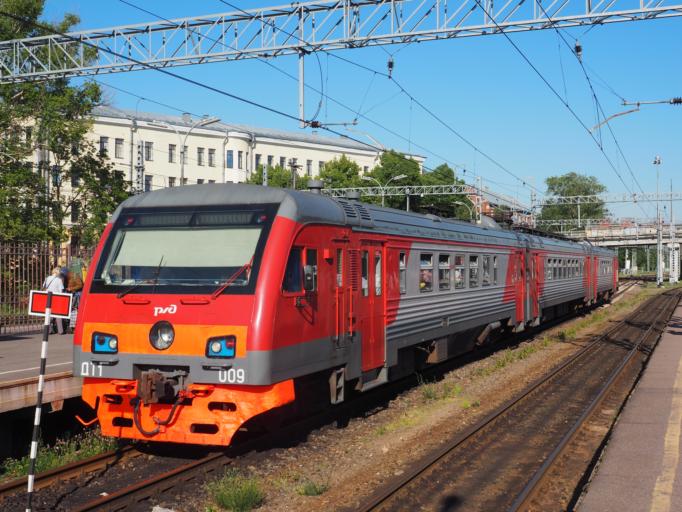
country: RU
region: Leningrad
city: Vyborg
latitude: 60.7155
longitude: 28.7545
